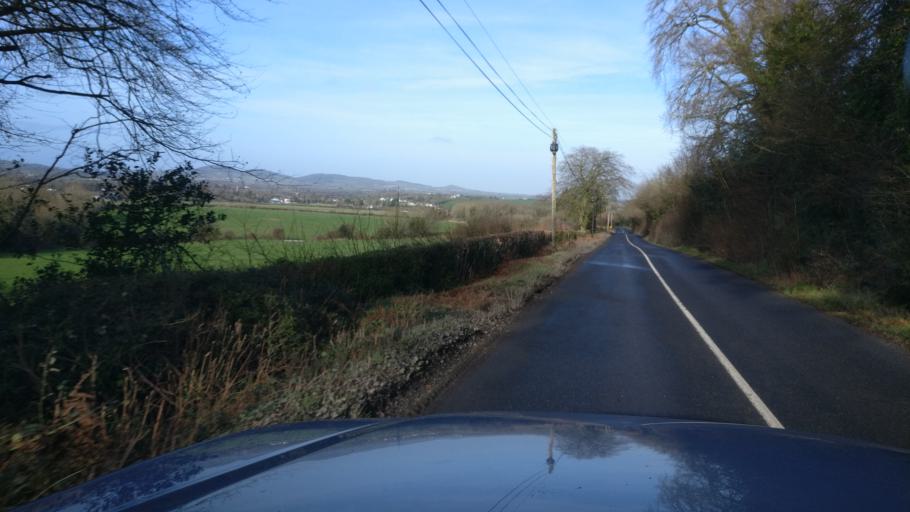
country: IE
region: Leinster
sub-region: Laois
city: Stradbally
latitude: 52.9473
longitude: -7.2002
